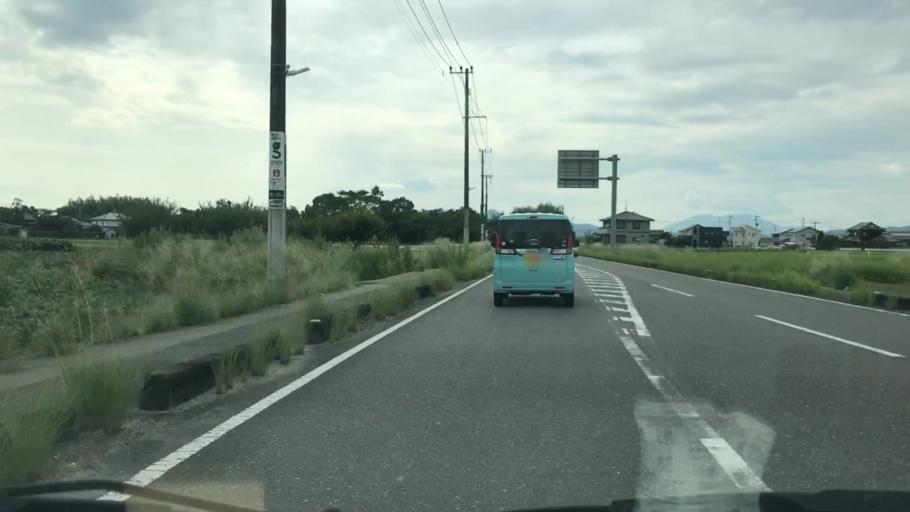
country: JP
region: Saga Prefecture
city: Saga-shi
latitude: 33.2759
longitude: 130.2600
